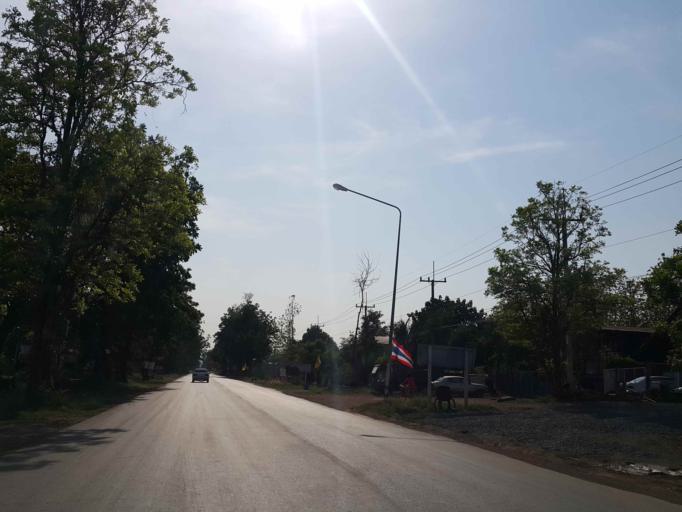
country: TH
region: Sukhothai
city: Thung Saliam
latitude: 17.3337
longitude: 99.5499
